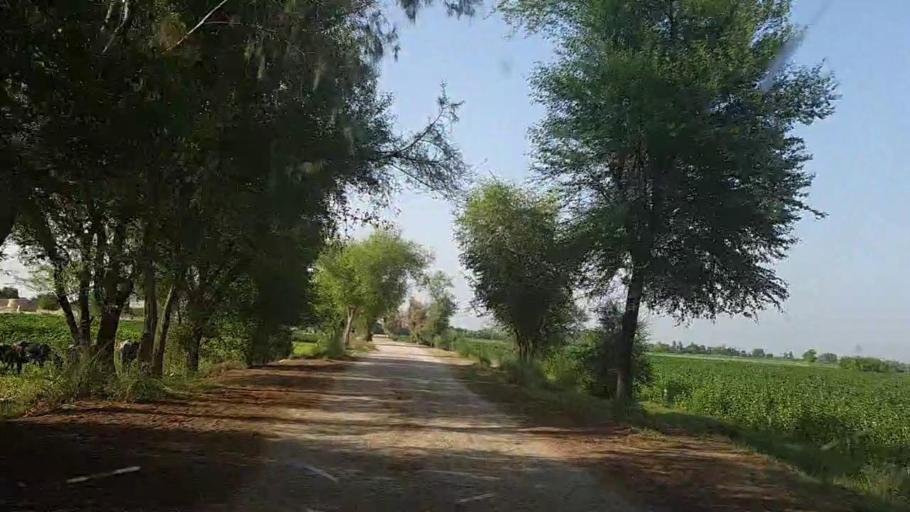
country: PK
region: Sindh
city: Khanpur
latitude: 27.7197
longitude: 69.3317
